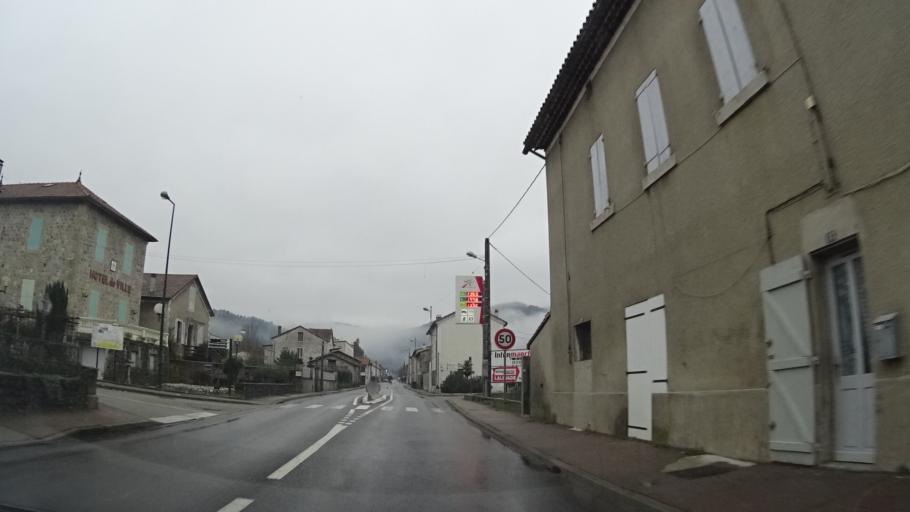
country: FR
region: Rhone-Alpes
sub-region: Departement de l'Ardeche
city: Labegude
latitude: 44.6498
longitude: 4.3228
